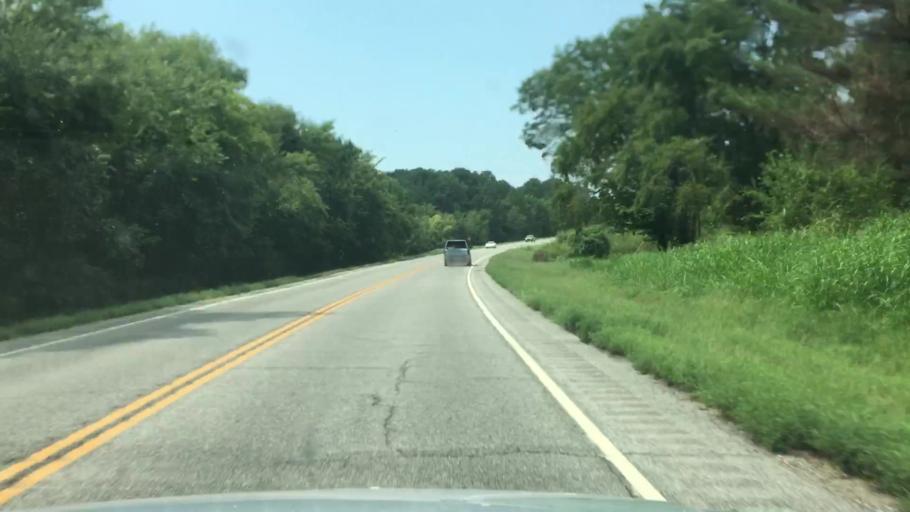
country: US
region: Oklahoma
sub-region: Muskogee County
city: Fort Gibson
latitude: 35.9303
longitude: -95.2352
